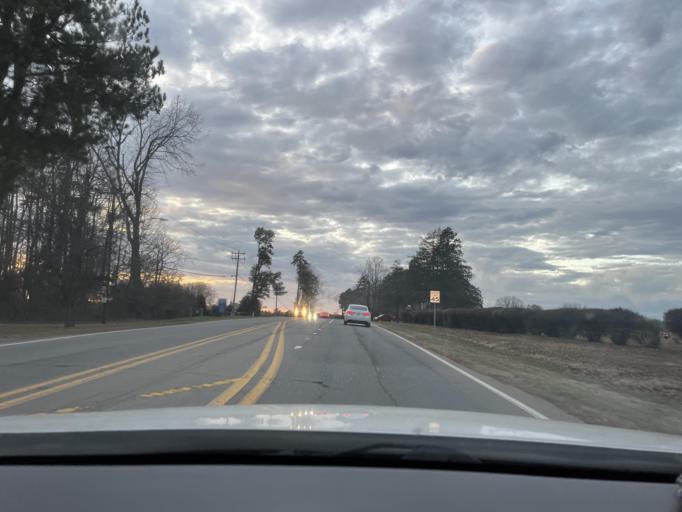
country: US
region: North Carolina
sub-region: Guilford County
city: Gibsonville
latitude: 36.0810
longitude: -79.5347
